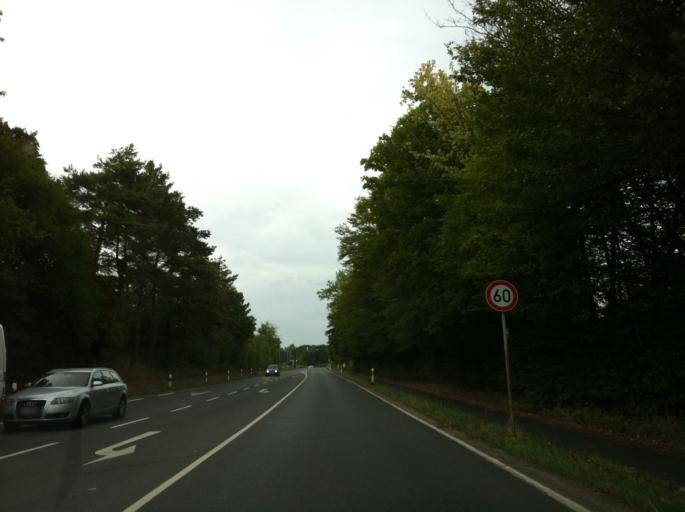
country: DE
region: Hesse
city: Sulzbach
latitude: 50.1385
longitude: 8.5180
